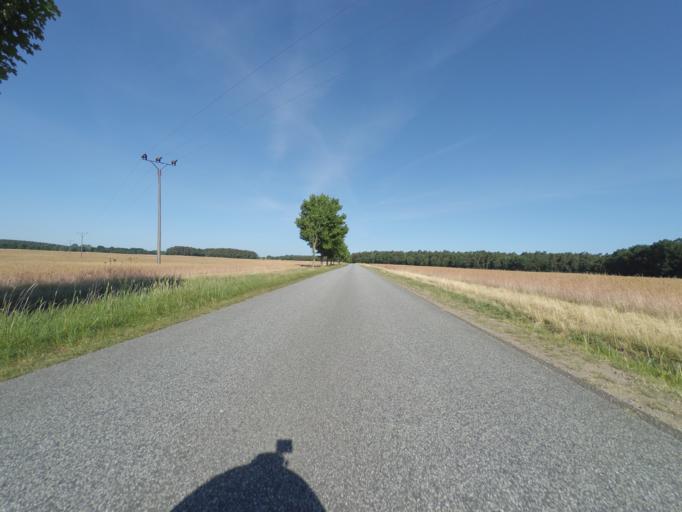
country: DE
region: Mecklenburg-Vorpommern
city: Lubz
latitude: 53.3759
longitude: 12.0594
